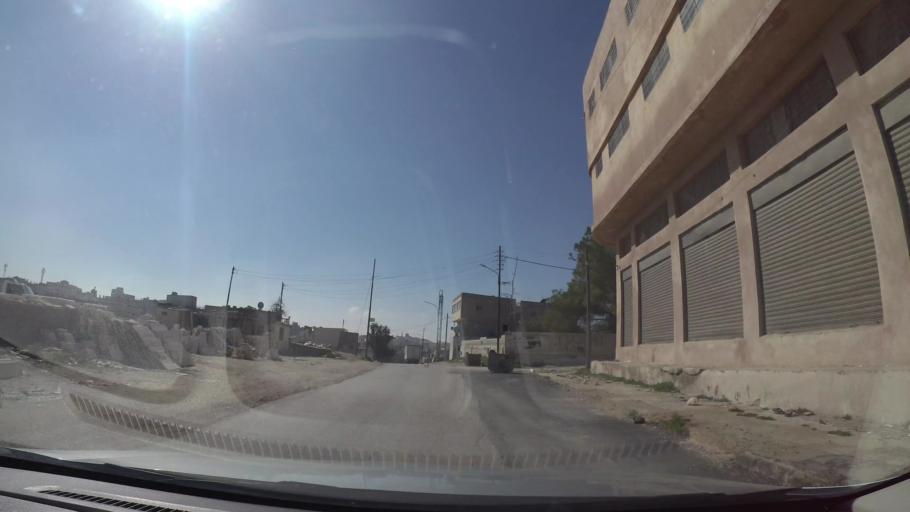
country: JO
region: Amman
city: Al Bunayyat ash Shamaliyah
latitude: 31.9118
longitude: 35.9040
